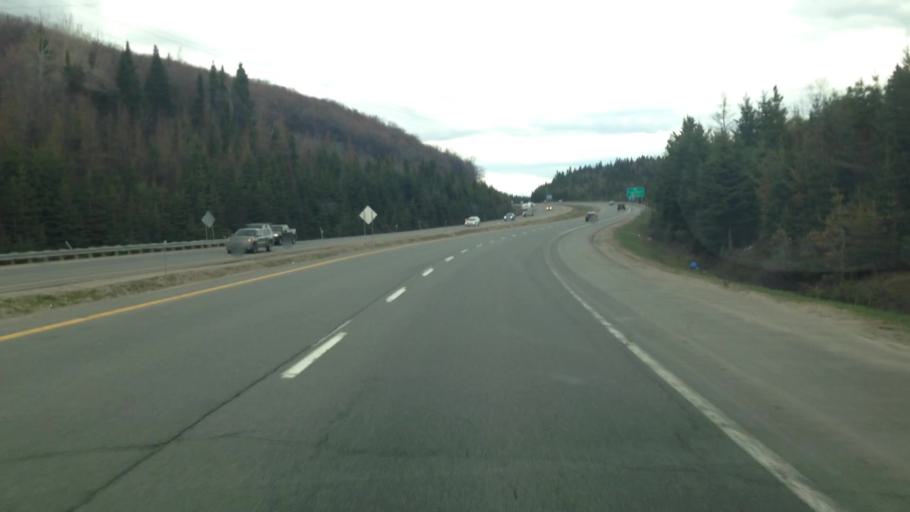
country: CA
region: Quebec
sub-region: Laurentides
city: Sainte-Agathe-des-Monts
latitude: 46.0281
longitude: -74.2626
